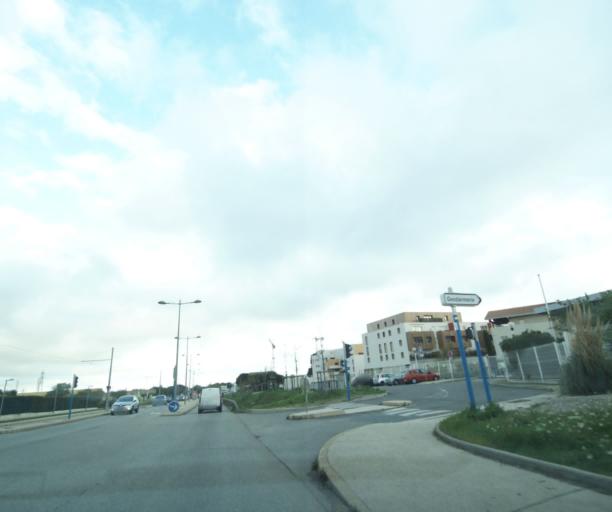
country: FR
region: Languedoc-Roussillon
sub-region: Departement de l'Herault
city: Saint-Jean-de-Vedas
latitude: 43.5737
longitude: 3.8326
